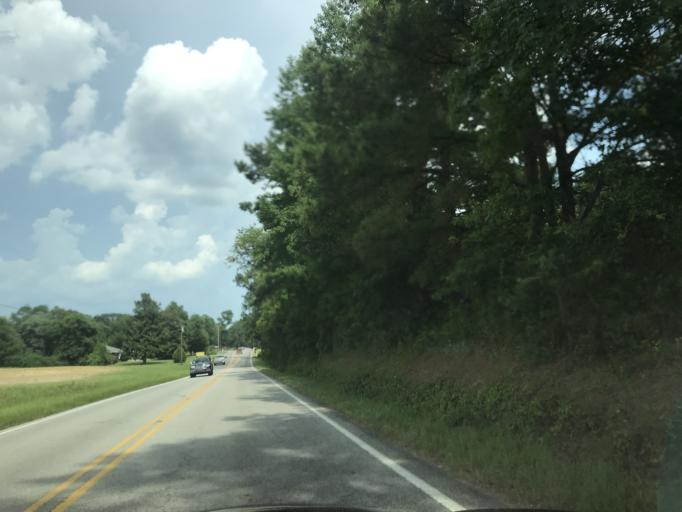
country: US
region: North Carolina
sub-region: Johnston County
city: Four Oaks
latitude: 35.5142
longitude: -78.5394
